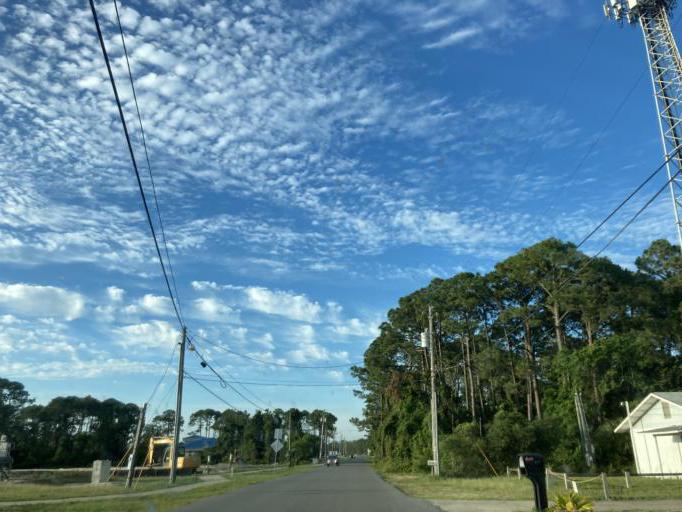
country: US
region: Florida
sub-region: Bay County
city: Panama City Beach
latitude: 30.1945
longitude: -85.8313
